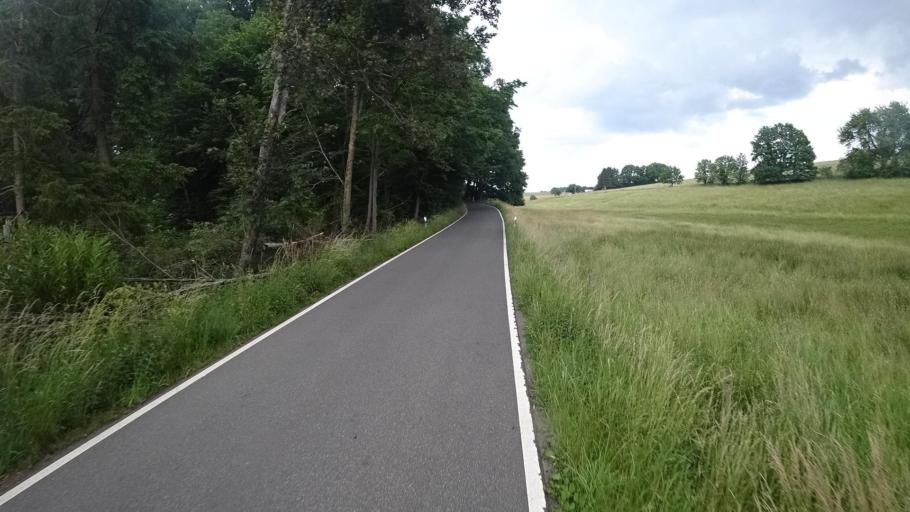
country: DE
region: Rheinland-Pfalz
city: Volkerzen
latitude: 50.7180
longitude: 7.6822
